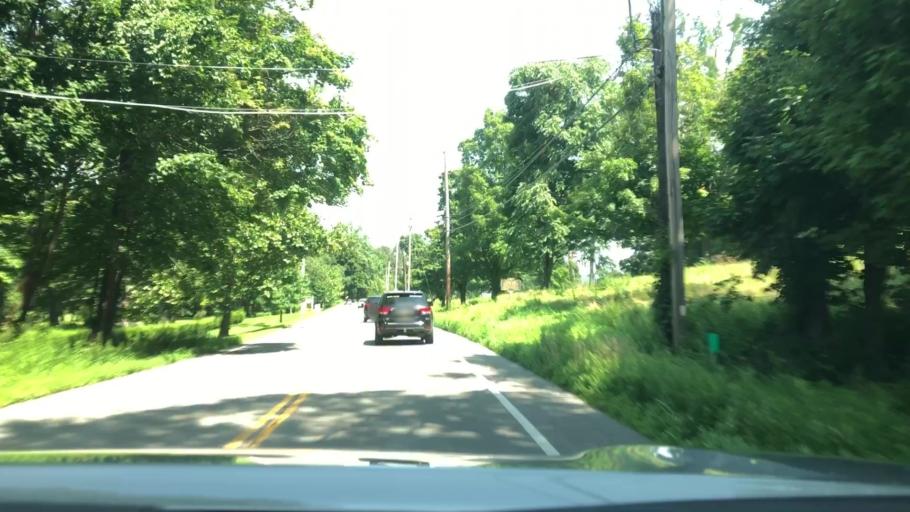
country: US
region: New York
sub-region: Orange County
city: Highland Falls
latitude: 41.3589
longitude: -73.9523
